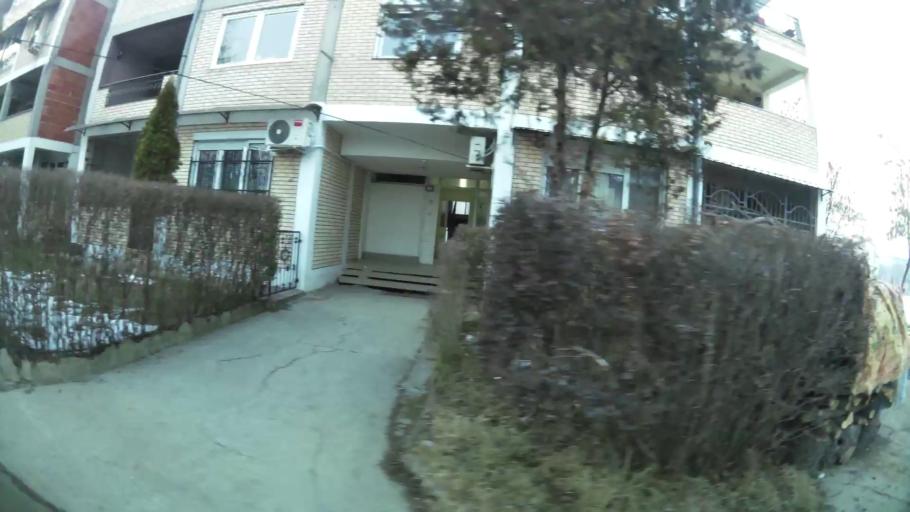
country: MK
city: Creshevo
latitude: 42.0060
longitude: 21.5073
